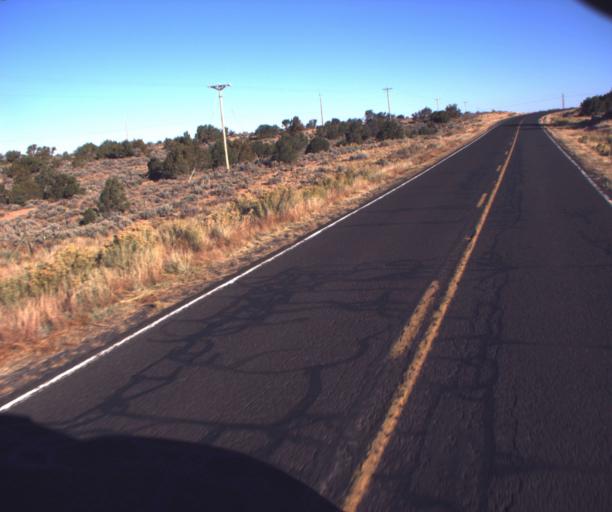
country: US
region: Arizona
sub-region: Apache County
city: Ganado
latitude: 35.6681
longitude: -109.5504
